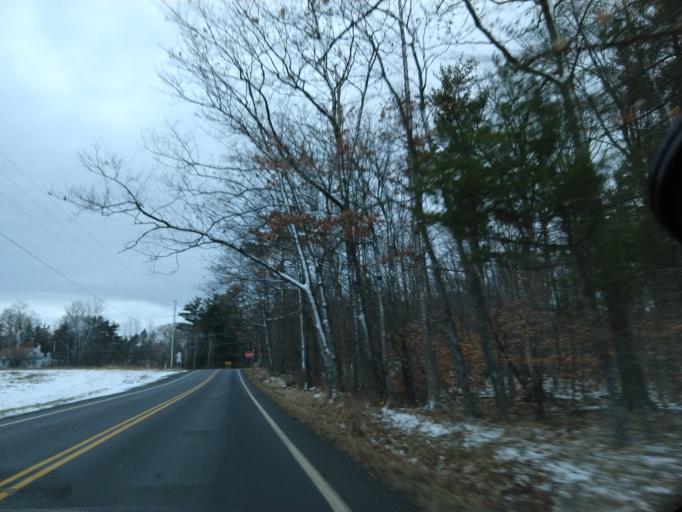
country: US
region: New York
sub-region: Tompkins County
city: Northeast Ithaca
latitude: 42.4669
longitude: -76.4476
